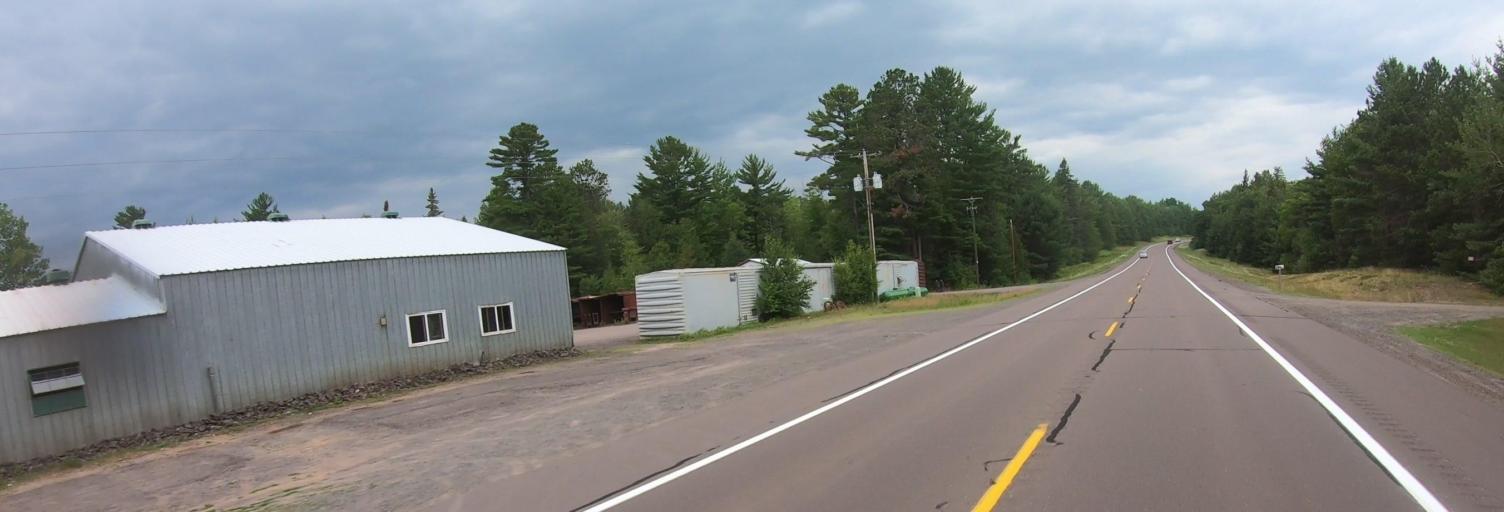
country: US
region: Michigan
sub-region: Baraga County
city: Baraga
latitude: 46.8243
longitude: -88.4831
